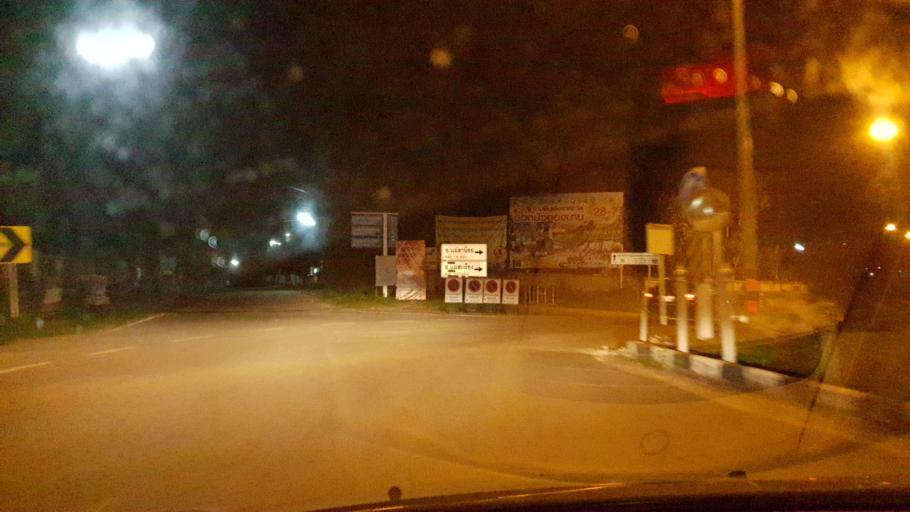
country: TH
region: Mae Hong Son
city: Khun Yuam
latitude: 18.8316
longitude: 97.9359
